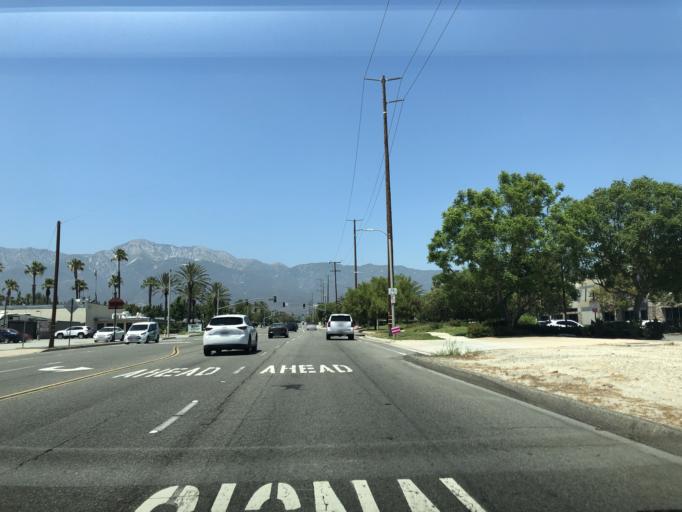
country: US
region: California
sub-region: San Bernardino County
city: Rancho Cucamonga
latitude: 34.0991
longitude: -117.5456
